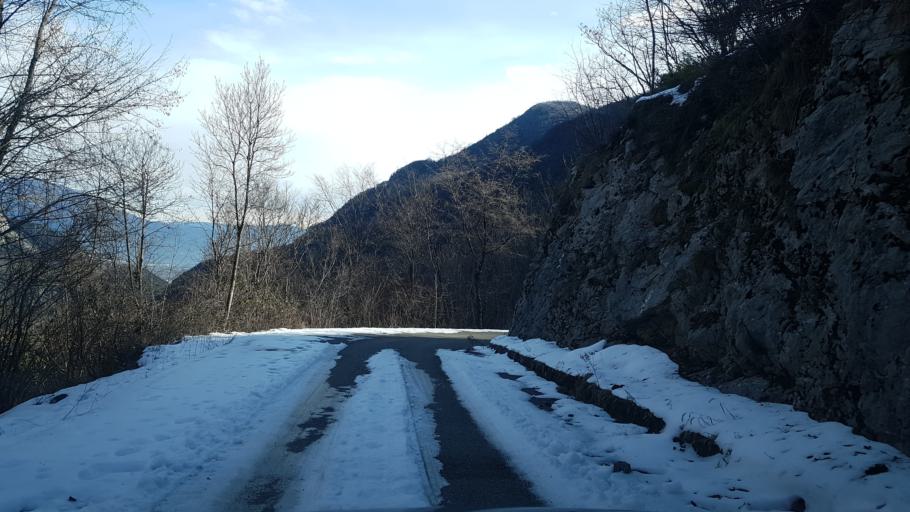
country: IT
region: Friuli Venezia Giulia
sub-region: Provincia di Udine
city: Trasaghis
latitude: 46.2920
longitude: 13.0315
